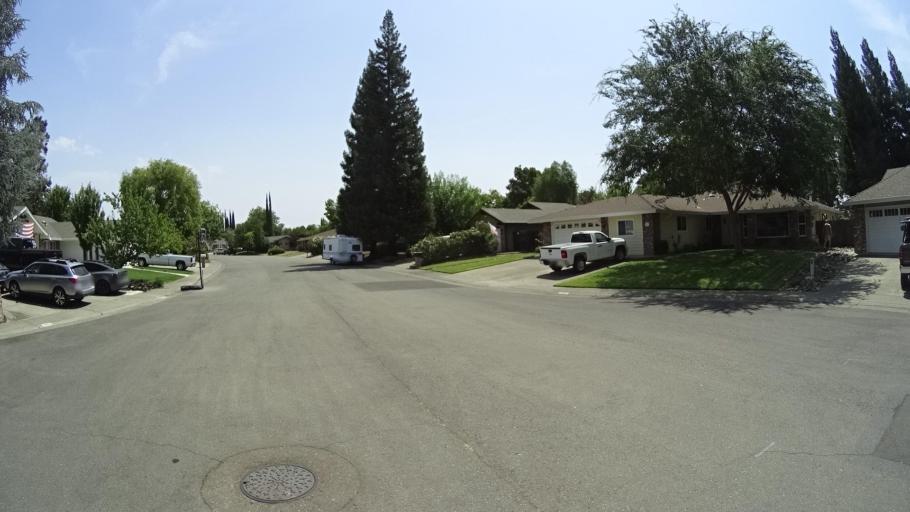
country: US
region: California
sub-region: Placer County
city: Rocklin
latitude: 38.7962
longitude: -121.2433
